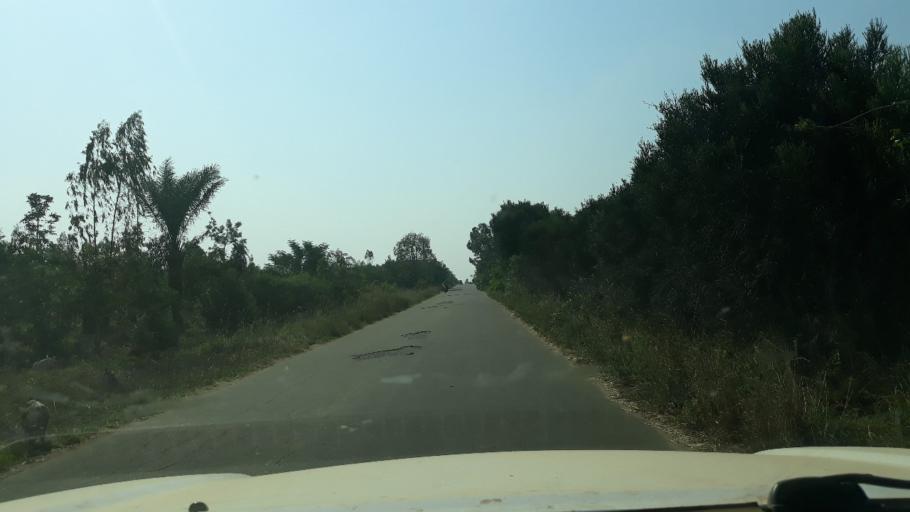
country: BI
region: Cibitoke
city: Cibitoke
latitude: -2.9679
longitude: 29.0839
